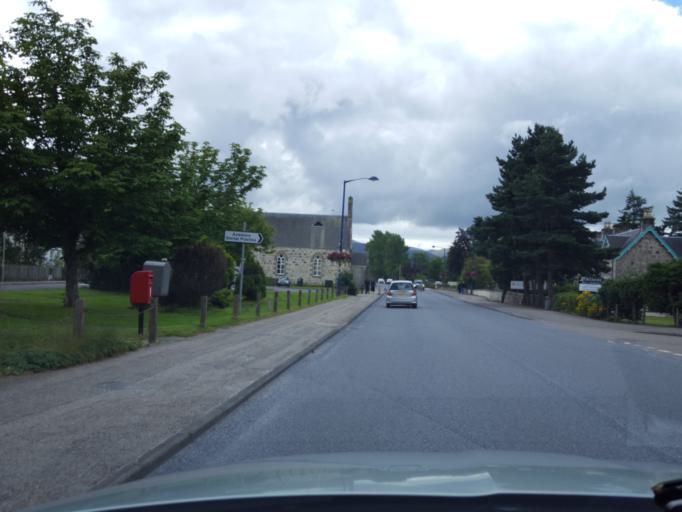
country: GB
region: Scotland
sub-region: Highland
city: Aviemore
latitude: 57.1954
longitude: -3.8291
